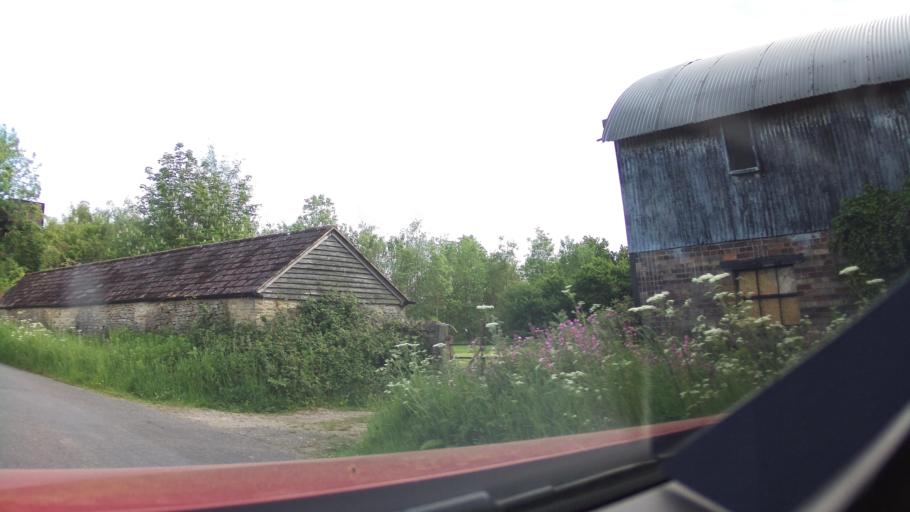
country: GB
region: England
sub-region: Gloucestershire
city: Chipping Campden
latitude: 52.0462
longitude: -1.7442
